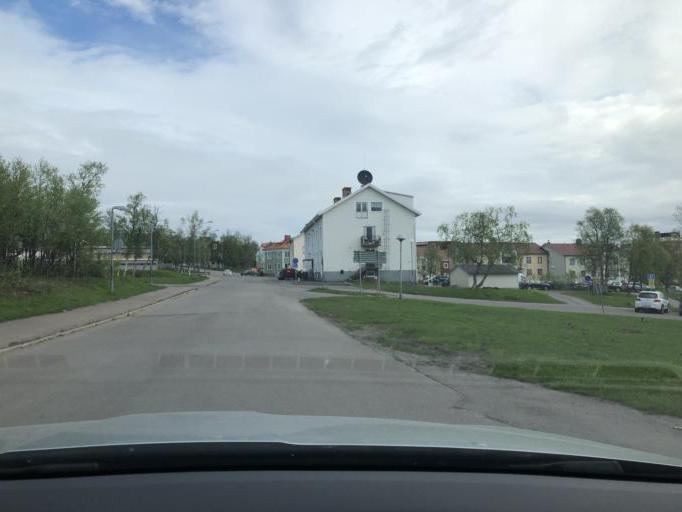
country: SE
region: Norrbotten
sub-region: Kiruna Kommun
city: Kiruna
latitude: 67.8506
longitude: 20.2358
